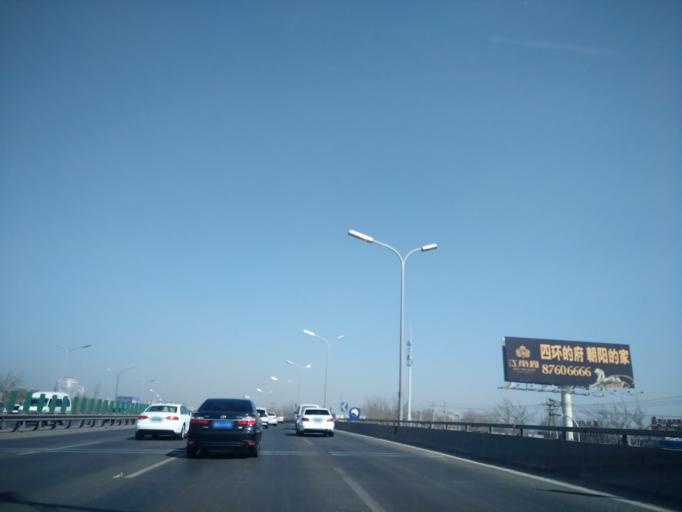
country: CN
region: Beijing
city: Jiugong
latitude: 39.8463
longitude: 116.4784
